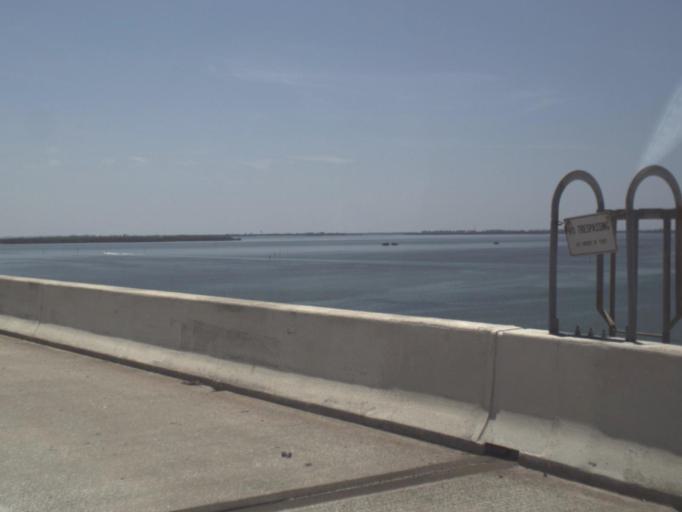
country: US
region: Florida
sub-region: Pinellas County
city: Tierra Verde
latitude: 27.6929
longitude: -82.6790
